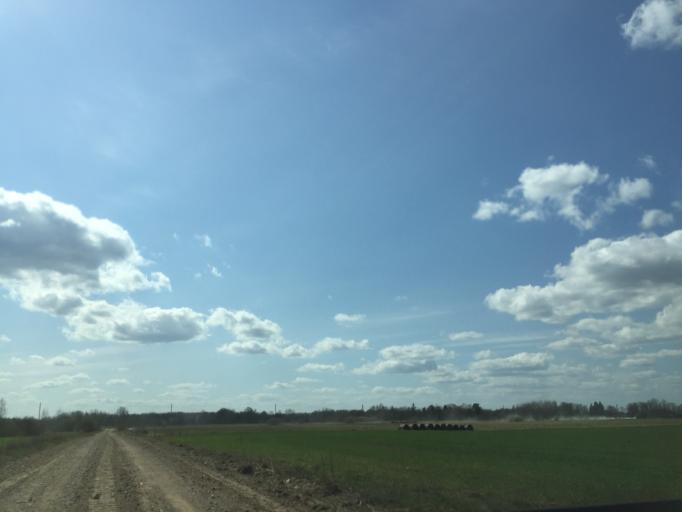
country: LV
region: Ogre
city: Jumprava
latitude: 56.7610
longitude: 25.0488
